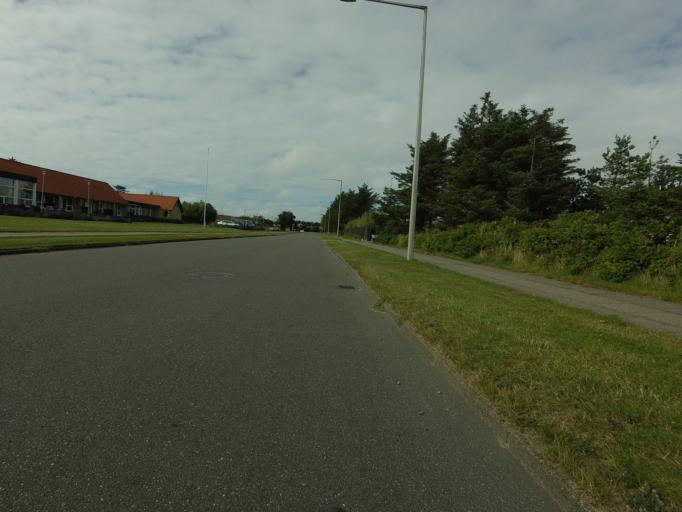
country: DK
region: North Denmark
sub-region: Jammerbugt Kommune
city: Pandrup
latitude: 57.3666
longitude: 9.7171
